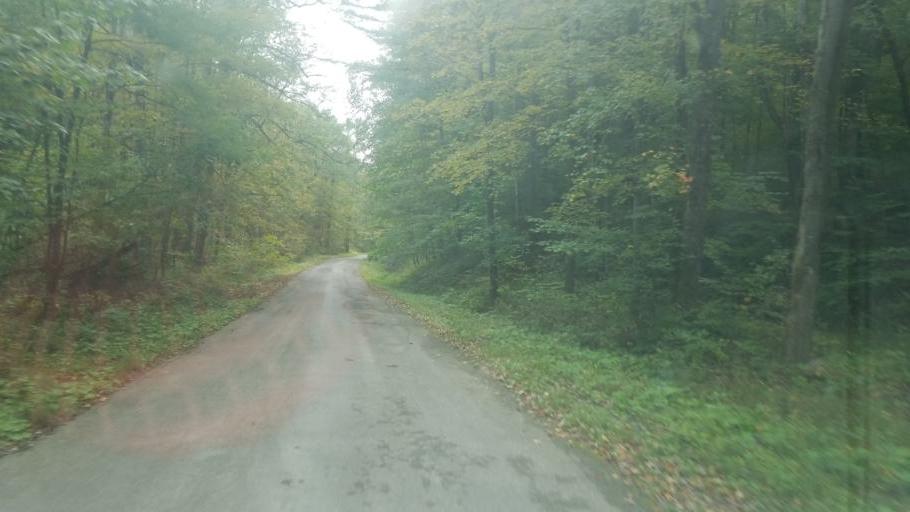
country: US
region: New York
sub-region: Allegany County
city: Cuba
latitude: 42.2212
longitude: -78.3408
